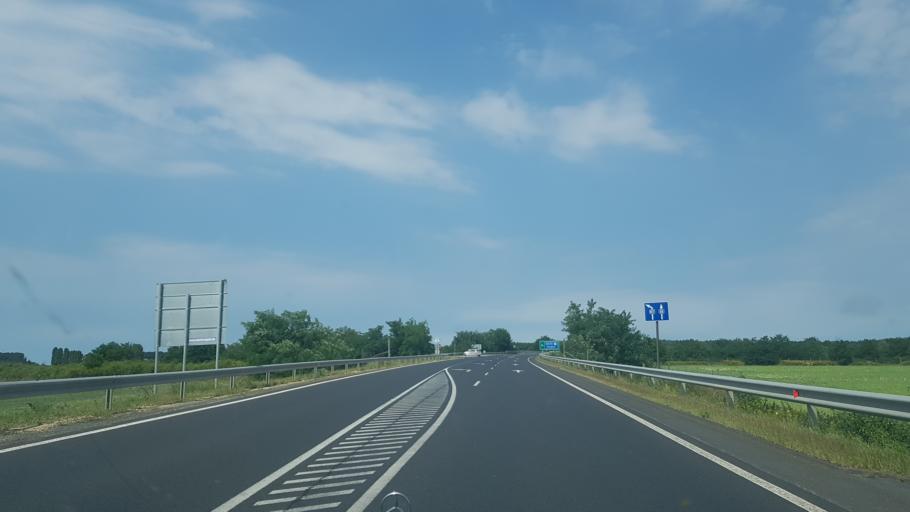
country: HU
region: Somogy
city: Kethely
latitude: 46.6695
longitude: 17.3529
